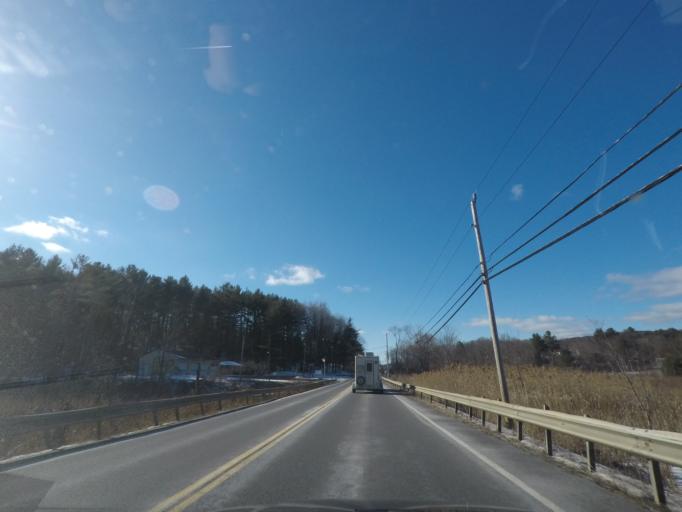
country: US
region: Massachusetts
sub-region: Berkshire County
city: Richmond
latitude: 42.4105
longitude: -73.4410
